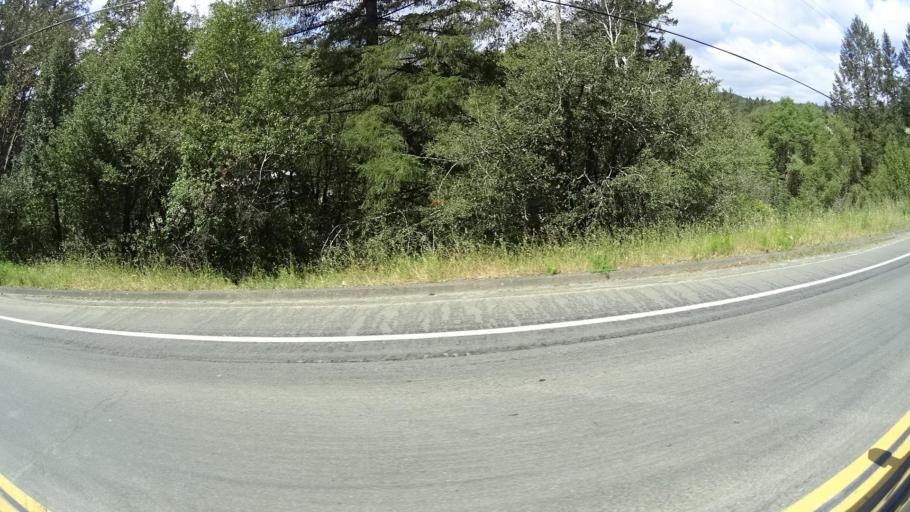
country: US
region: California
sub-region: Humboldt County
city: Redway
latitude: 40.1125
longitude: -123.7945
